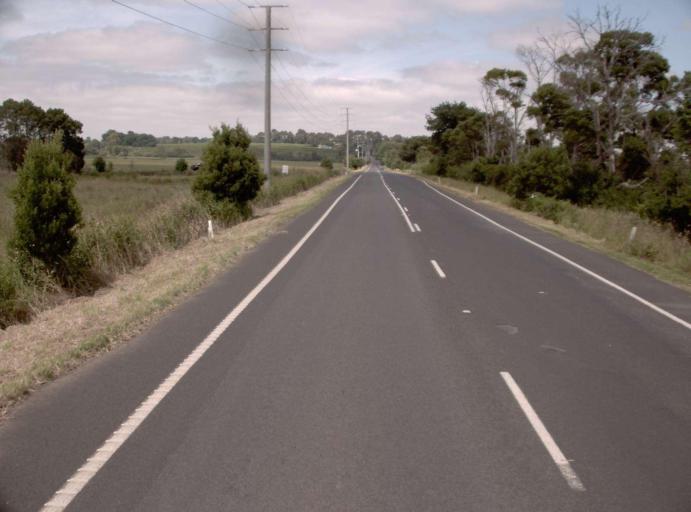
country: AU
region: Victoria
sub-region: Baw Baw
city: Warragul
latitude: -38.4568
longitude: 145.9732
